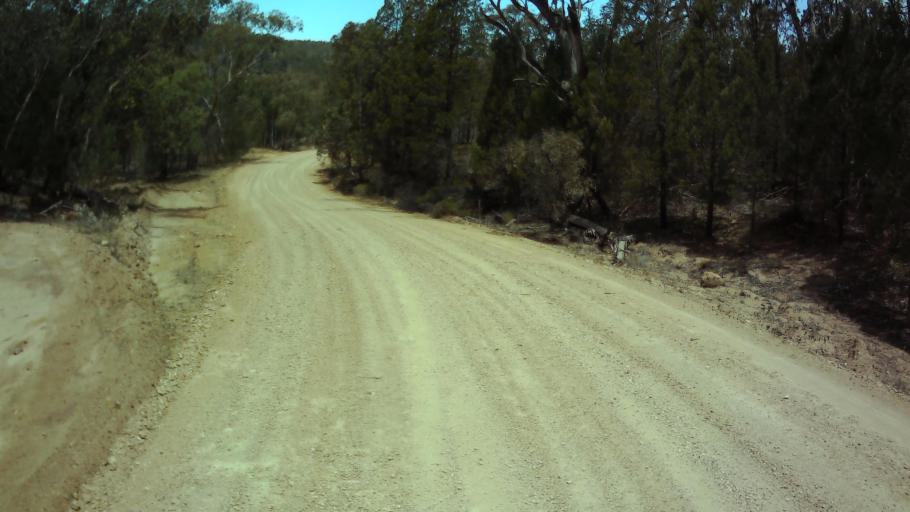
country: AU
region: New South Wales
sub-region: Weddin
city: Grenfell
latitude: -33.8137
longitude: 148.1626
